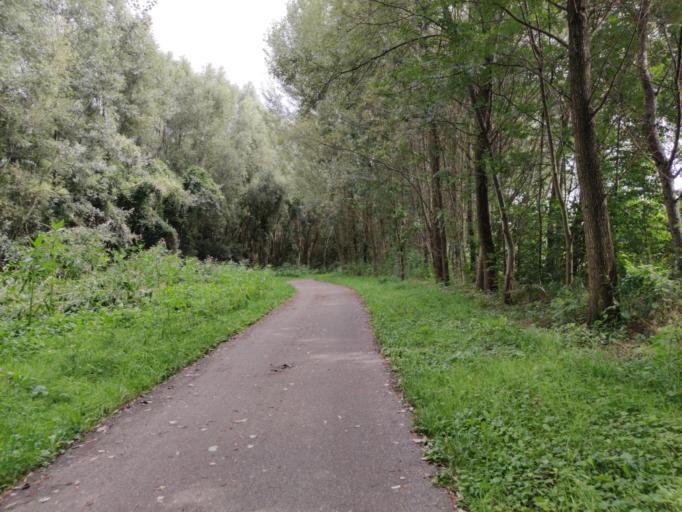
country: AT
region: Lower Austria
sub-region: Politischer Bezirk Melk
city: Ybbs an der Donau
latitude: 48.1676
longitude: 15.1003
